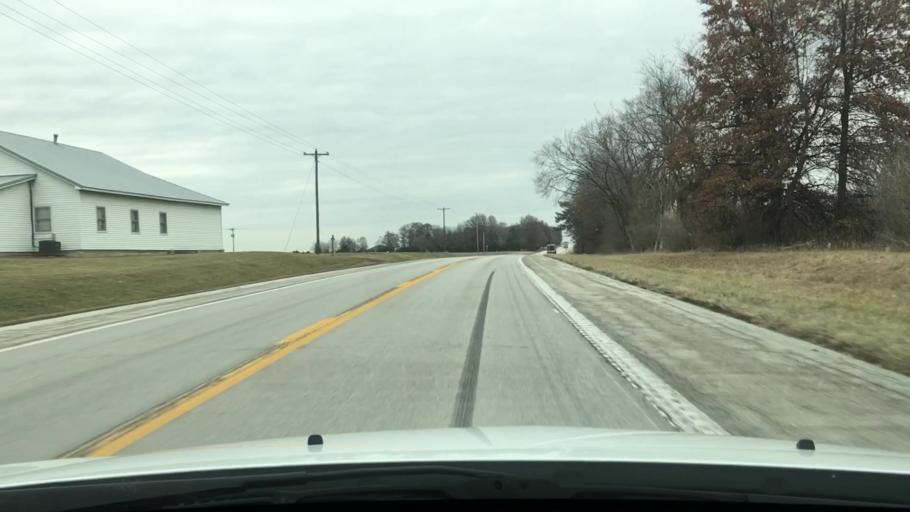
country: US
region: Missouri
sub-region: Montgomery County
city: Wellsville
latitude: 39.2052
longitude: -91.6466
